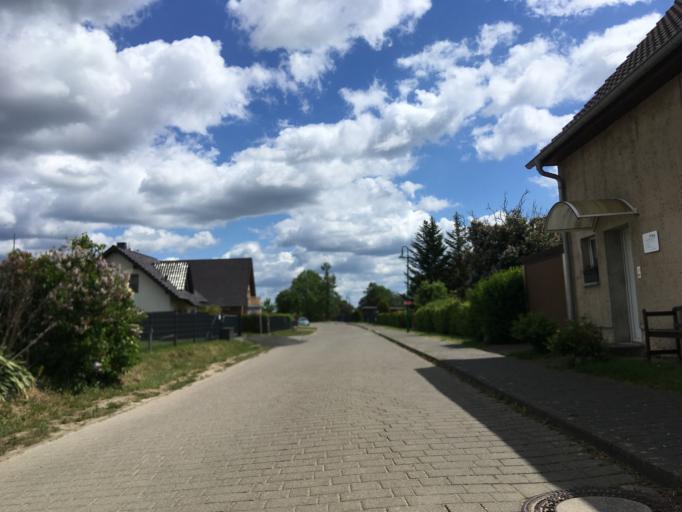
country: DE
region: Brandenburg
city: Liebenwalde
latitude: 52.8768
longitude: 13.4031
